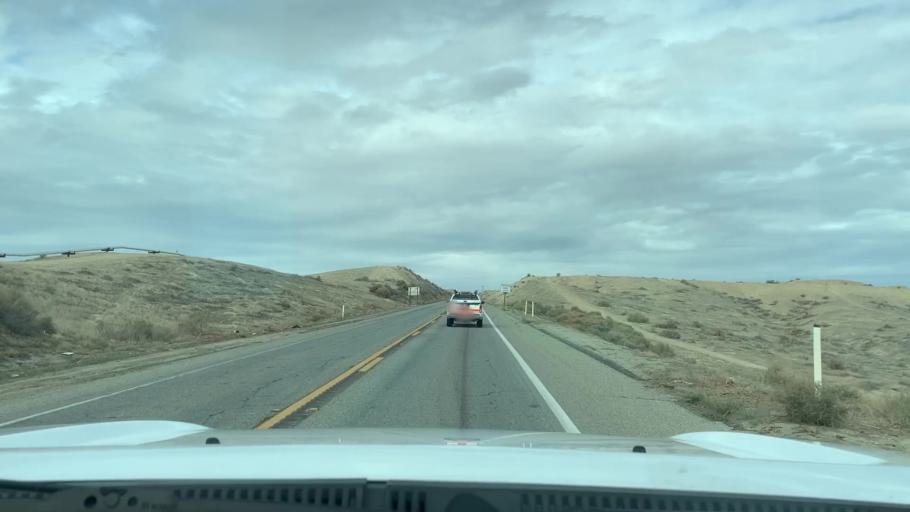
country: US
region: California
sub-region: Kern County
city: Maricopa
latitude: 35.0966
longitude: -119.4115
